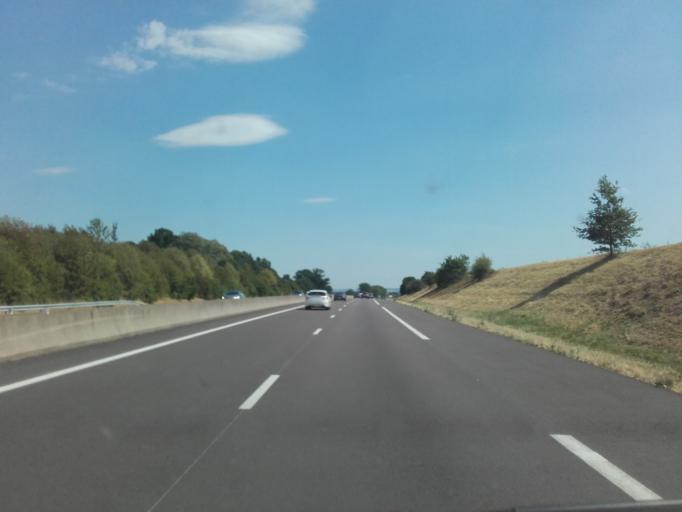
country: FR
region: Bourgogne
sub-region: Departement de la Cote-d'Or
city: Semur-en-Auxois
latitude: 47.4192
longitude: 4.3291
